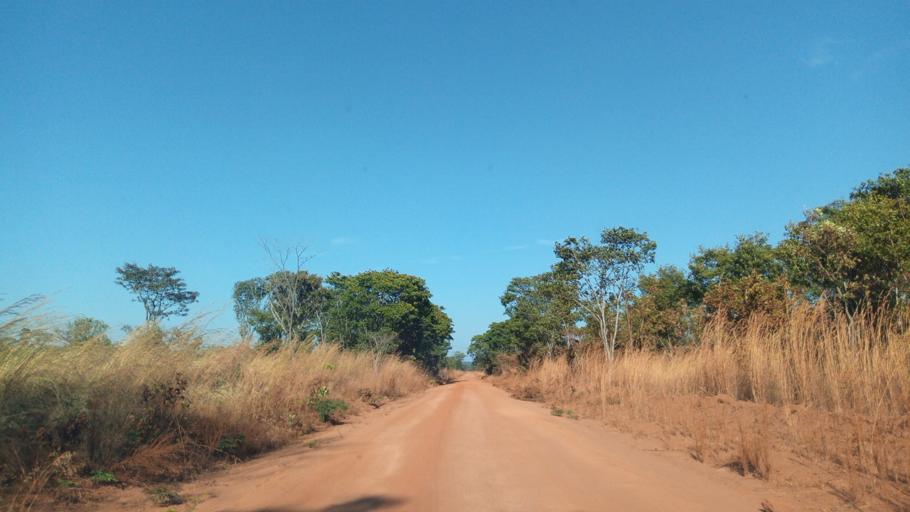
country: ZM
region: Luapula
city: Mwense
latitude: -10.5996
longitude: 28.4261
